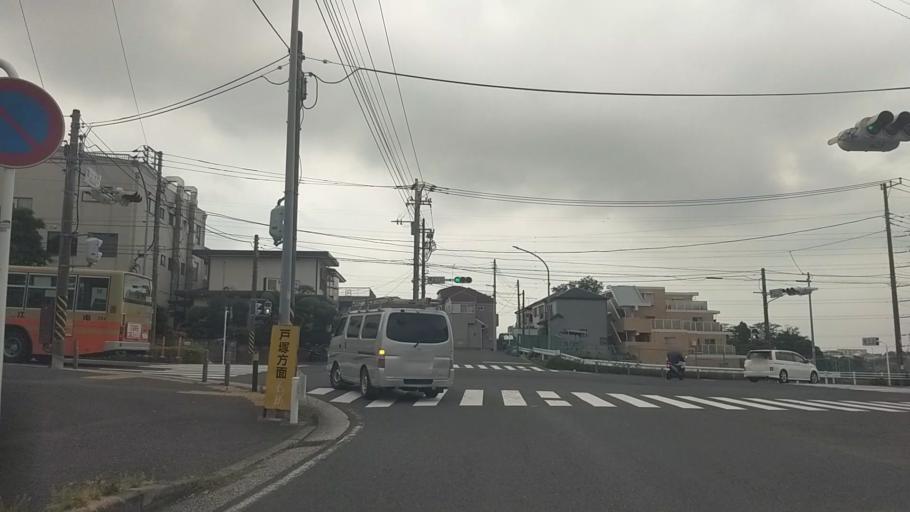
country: JP
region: Kanagawa
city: Kamakura
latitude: 35.3801
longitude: 139.5403
